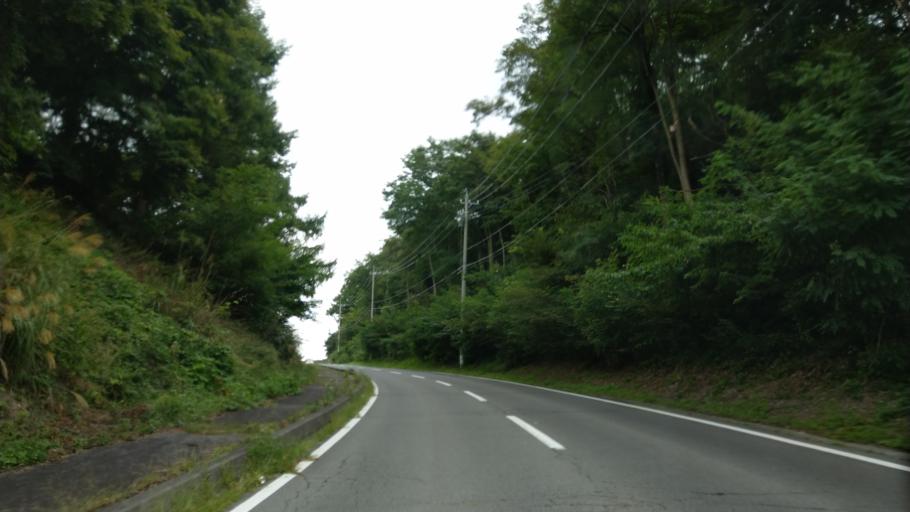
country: JP
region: Nagano
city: Komoro
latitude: 36.3246
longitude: 138.3946
